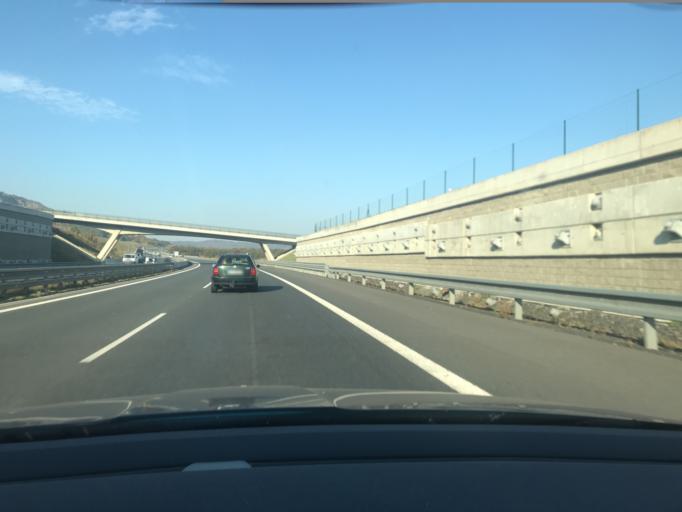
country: CZ
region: Ustecky
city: Velemin
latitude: 50.5502
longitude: 14.0108
